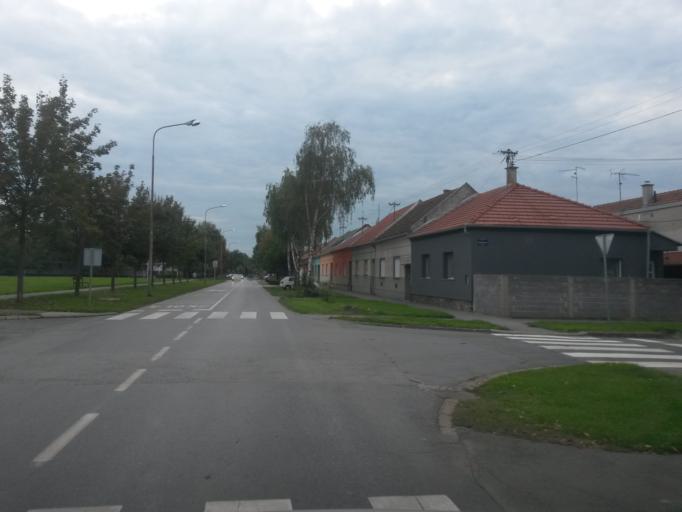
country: HR
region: Osjecko-Baranjska
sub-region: Grad Osijek
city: Osijek
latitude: 45.5485
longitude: 18.6850
